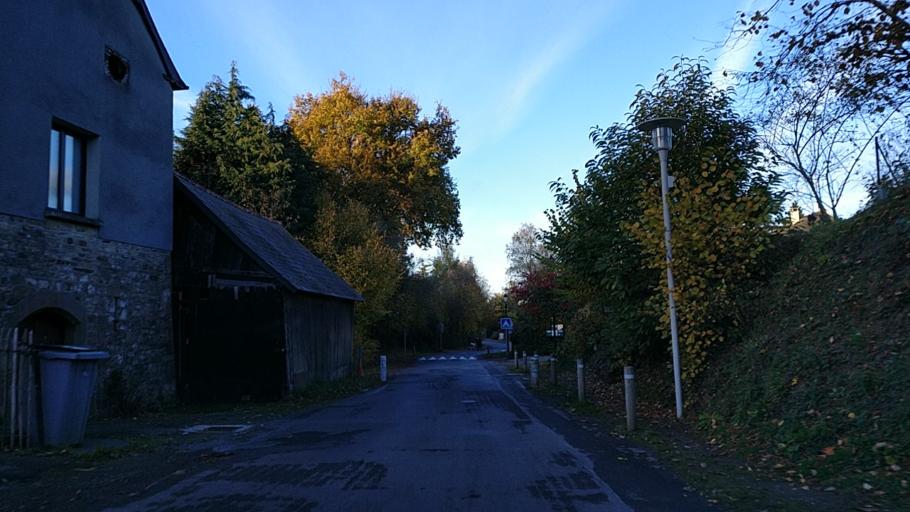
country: FR
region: Brittany
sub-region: Departement d'Ille-et-Vilaine
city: Saint-Sulpice-la-Foret
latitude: 48.2151
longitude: -1.5791
